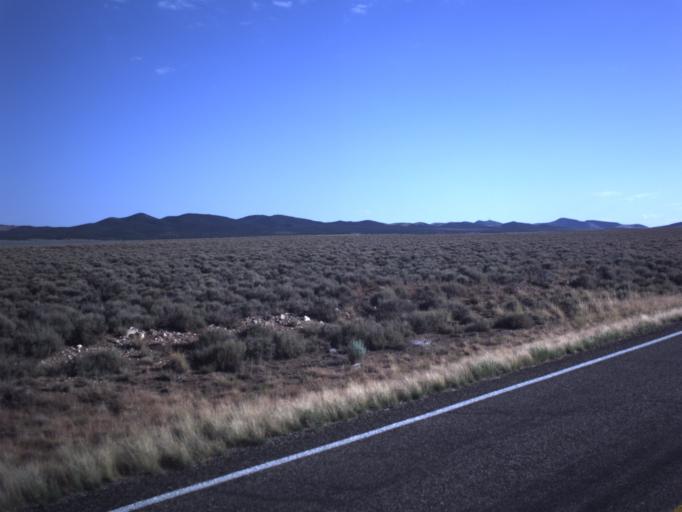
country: US
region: Utah
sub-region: Iron County
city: Enoch
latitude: 37.9538
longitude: -113.0131
